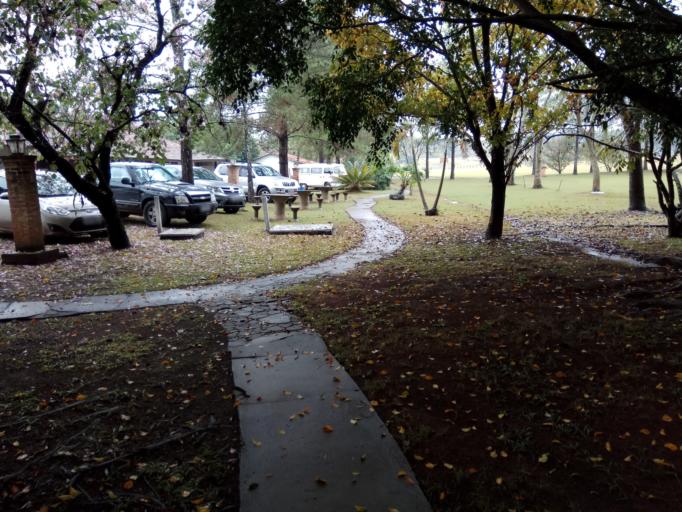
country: BR
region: Sao Paulo
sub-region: Charqueada
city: Charqueada
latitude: -22.4130
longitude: -47.7088
